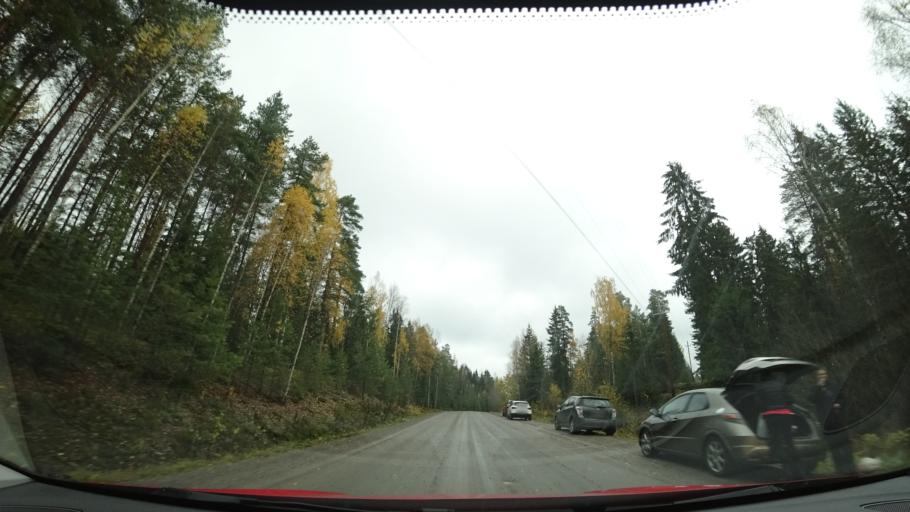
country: FI
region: Uusimaa
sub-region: Helsinki
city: Sibbo
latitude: 60.2907
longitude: 25.1957
